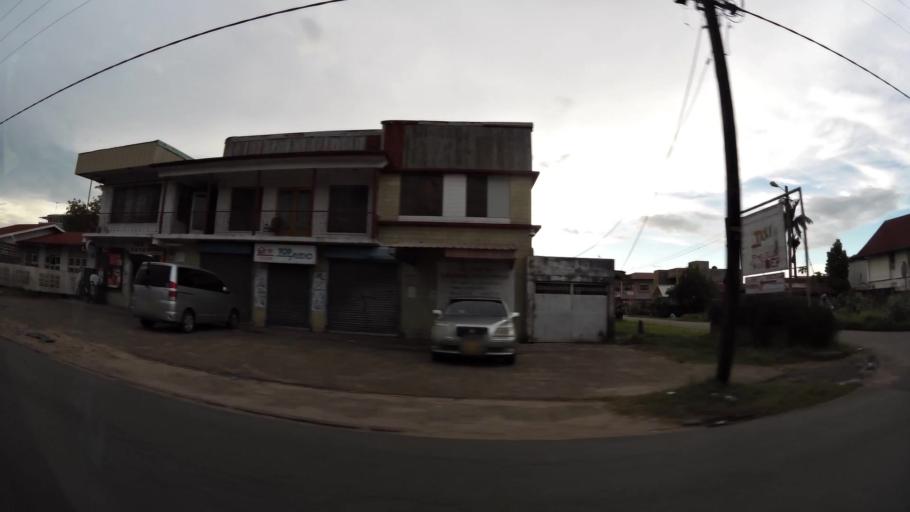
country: SR
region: Paramaribo
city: Paramaribo
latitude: 5.8347
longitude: -55.1433
